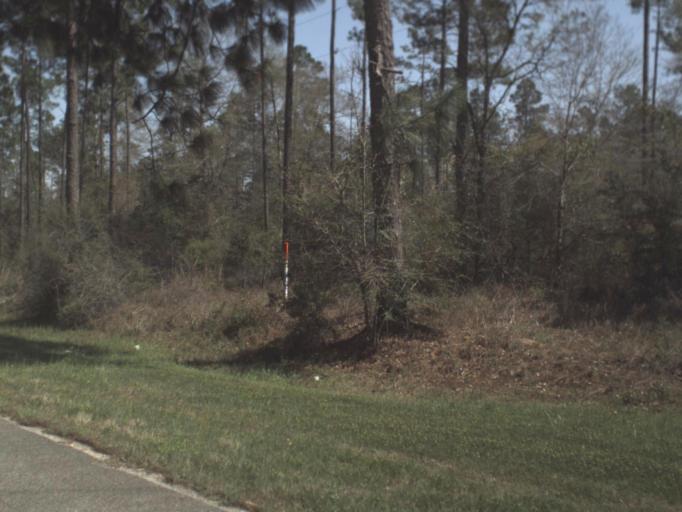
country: US
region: Florida
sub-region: Calhoun County
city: Blountstown
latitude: 30.4277
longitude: -85.1124
